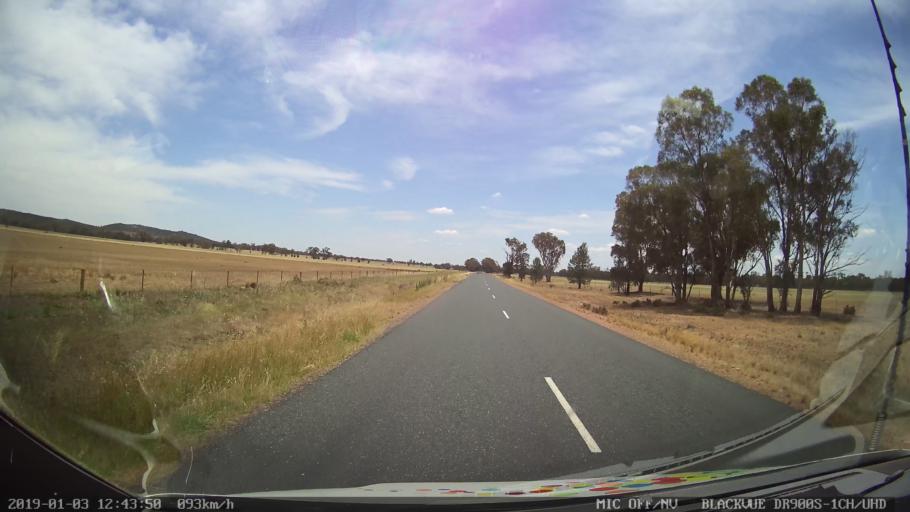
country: AU
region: New South Wales
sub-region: Weddin
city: Grenfell
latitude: -33.7698
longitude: 148.2145
